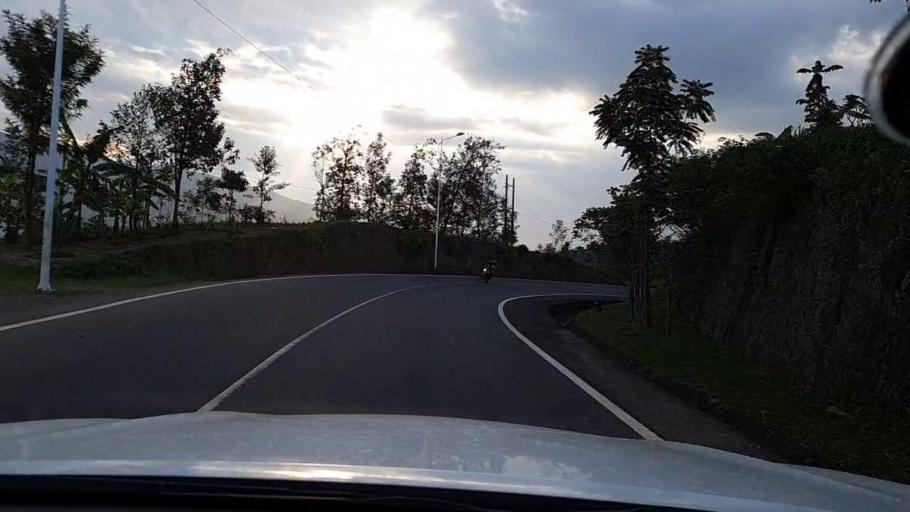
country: RW
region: Western Province
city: Kibuye
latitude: -2.0868
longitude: 29.4108
